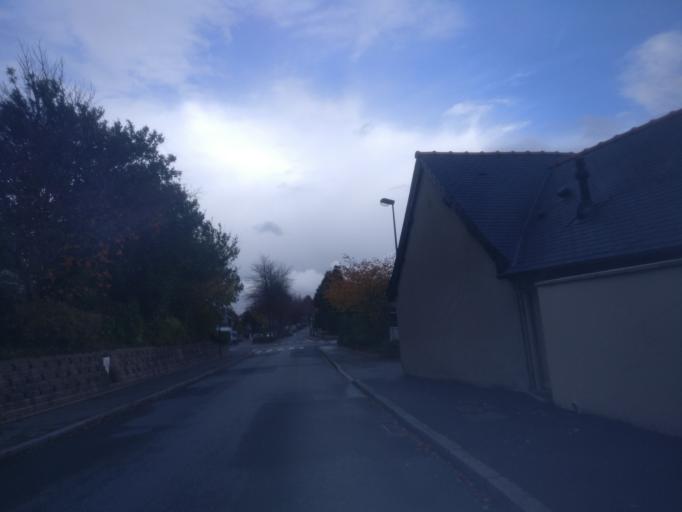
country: FR
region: Brittany
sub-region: Departement d'Ille-et-Vilaine
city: Breal-sous-Montfort
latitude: 48.0475
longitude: -1.8611
